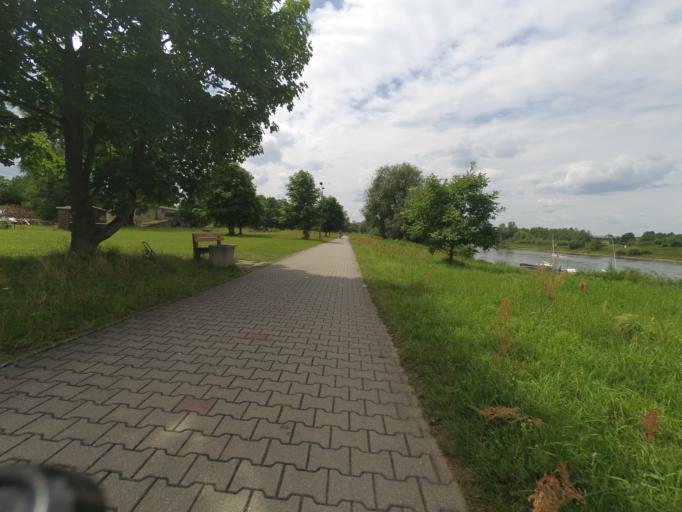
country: DE
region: Saxony
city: Pirna
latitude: 50.9635
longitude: 13.9248
